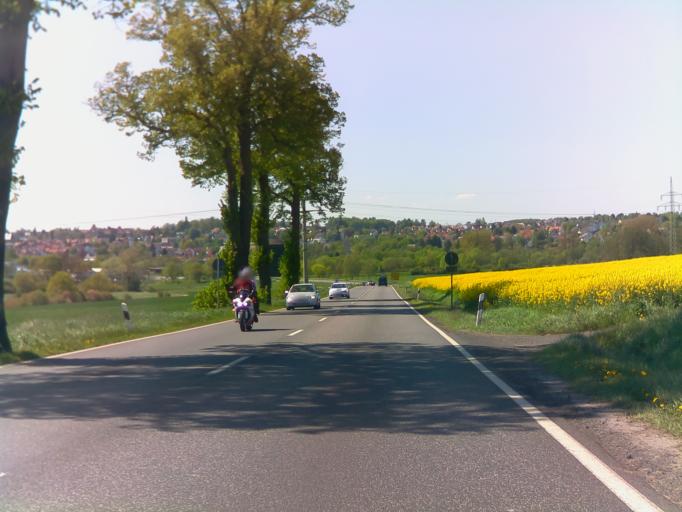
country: DE
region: Hesse
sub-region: Regierungsbezirk Giessen
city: Alsfeld
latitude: 50.7507
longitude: 9.2969
